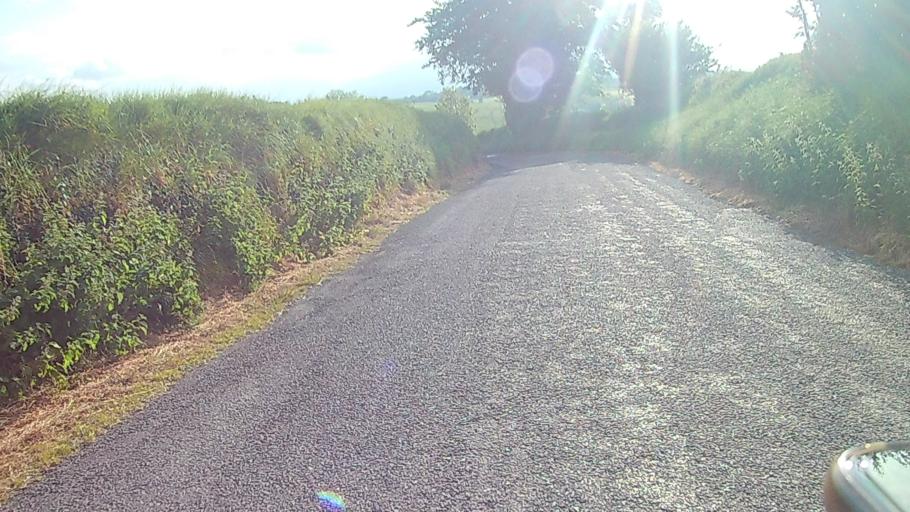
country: IE
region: Munster
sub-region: County Cork
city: Cork
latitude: 51.9777
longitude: -8.4598
